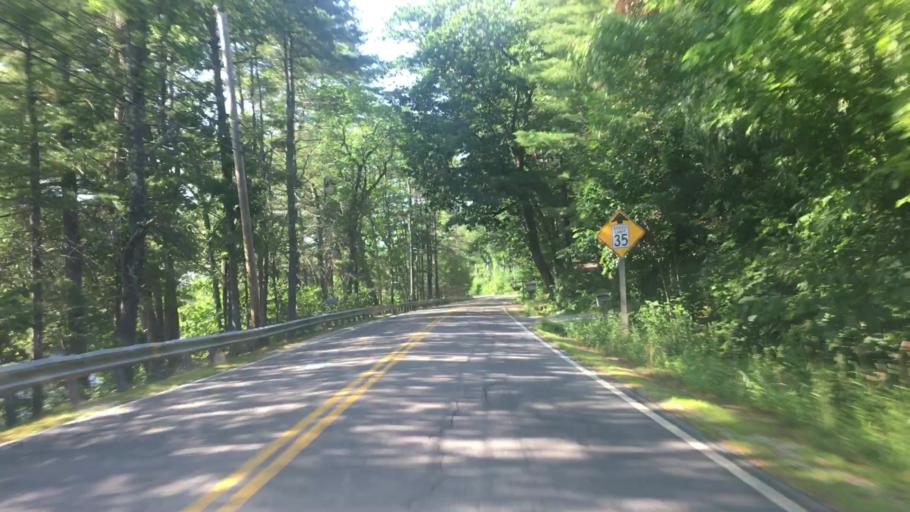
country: US
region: Maine
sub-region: York County
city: Hollis Center
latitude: 43.6595
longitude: -70.5972
